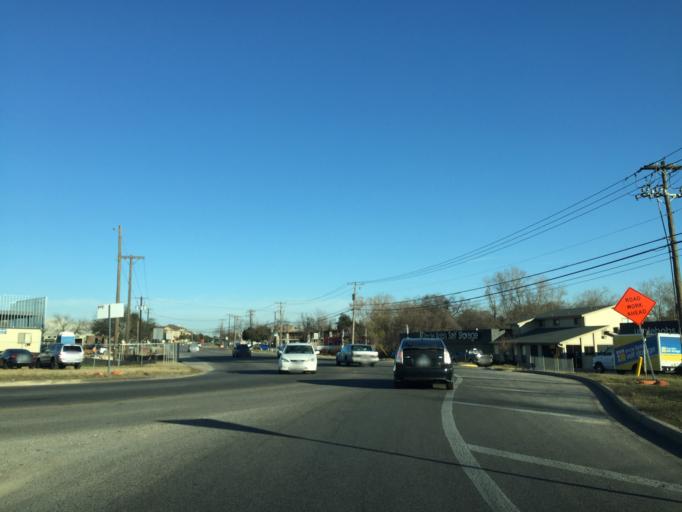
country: US
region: Texas
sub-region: Williamson County
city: Jollyville
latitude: 30.4352
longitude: -97.7702
